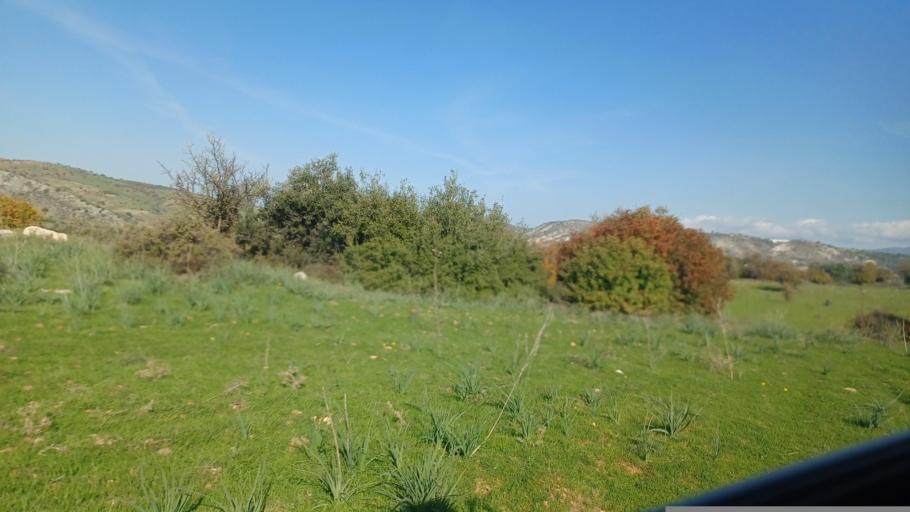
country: CY
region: Pafos
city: Mesogi
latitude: 34.7643
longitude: 32.5605
